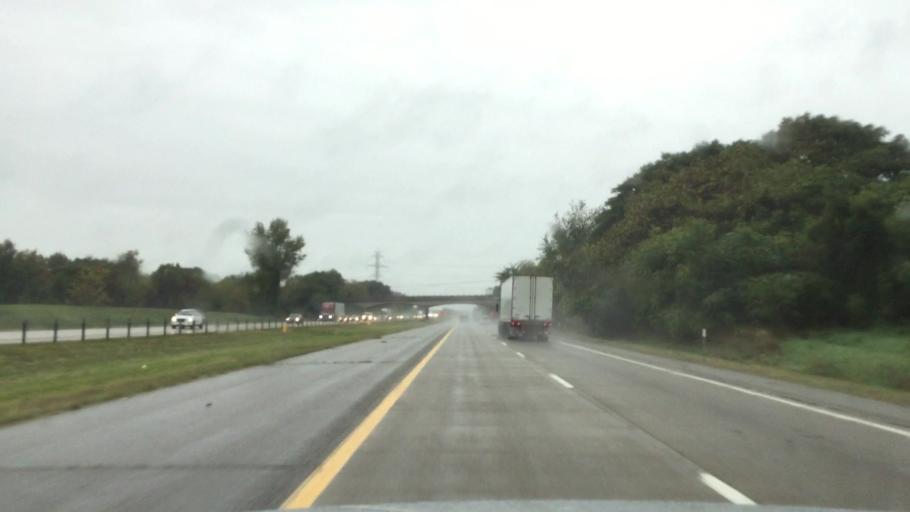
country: US
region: Michigan
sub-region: Berrien County
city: Coloma
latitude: 42.1646
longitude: -86.3273
